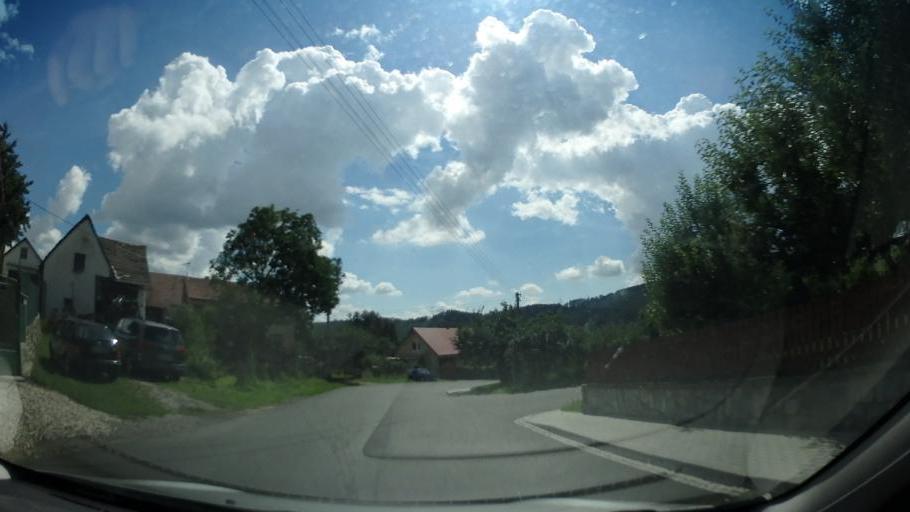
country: CZ
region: Olomoucky
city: Zabreh
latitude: 49.8741
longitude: 16.8481
